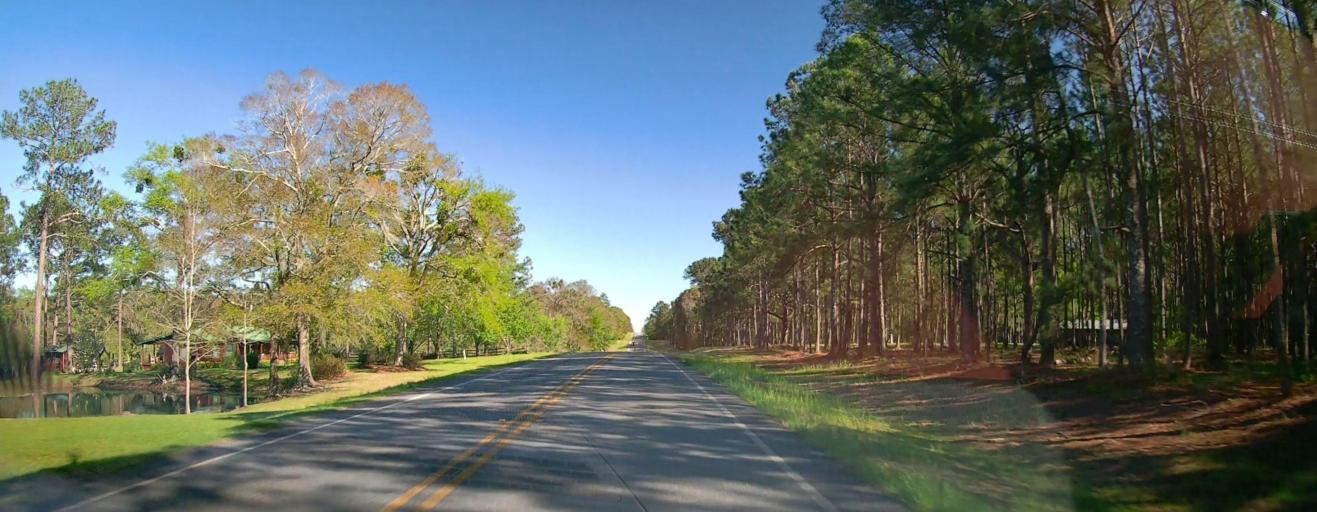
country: US
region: Georgia
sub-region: Wilcox County
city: Rochelle
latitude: 32.0078
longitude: -83.4885
